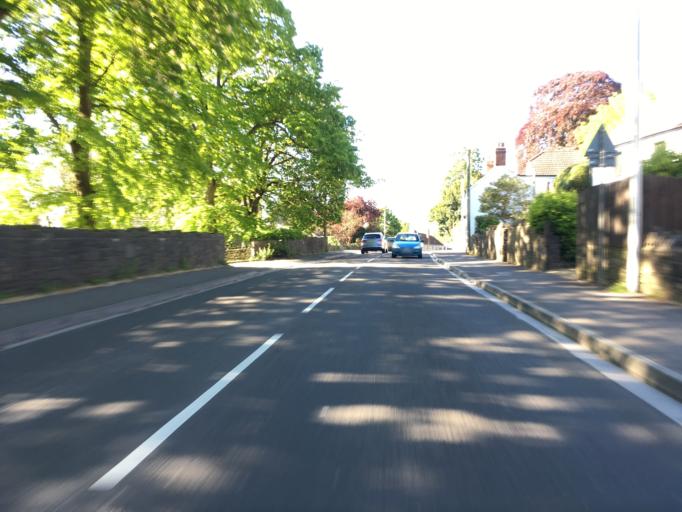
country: GB
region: England
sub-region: North Somerset
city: Clevedon
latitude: 51.4413
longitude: -2.8417
